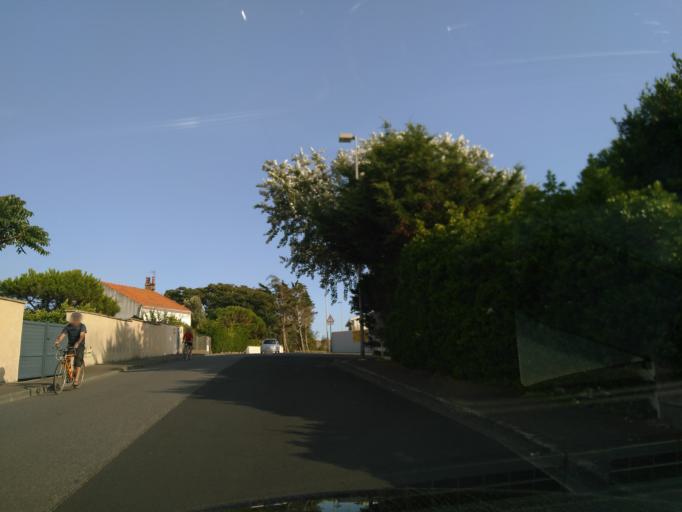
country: FR
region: Pays de la Loire
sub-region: Departement de la Vendee
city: Les Sables-d'Olonne
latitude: 46.5010
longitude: -1.8046
